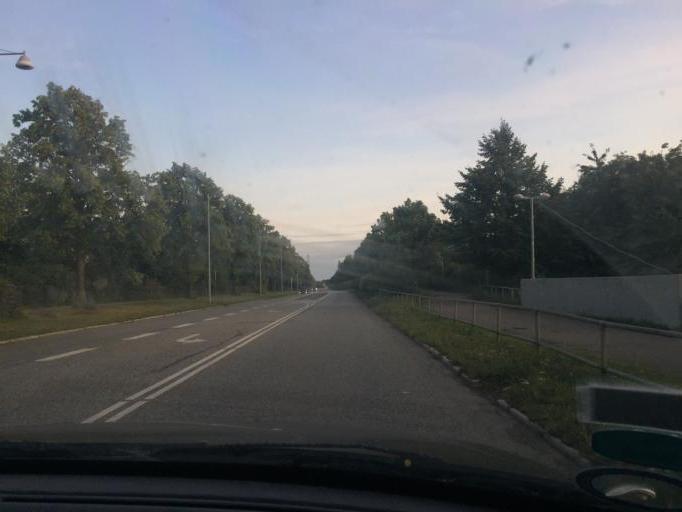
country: DK
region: Capital Region
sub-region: Albertslund Kommune
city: Albertslund
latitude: 55.6704
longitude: 12.3399
